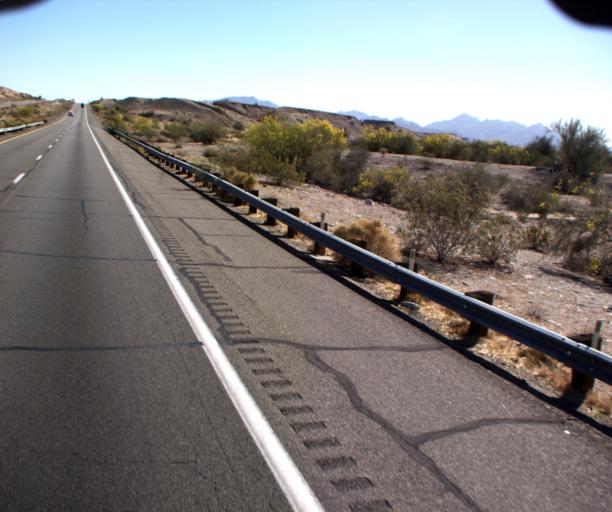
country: US
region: Arizona
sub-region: La Paz County
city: Ehrenberg
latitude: 33.6046
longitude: -114.5016
